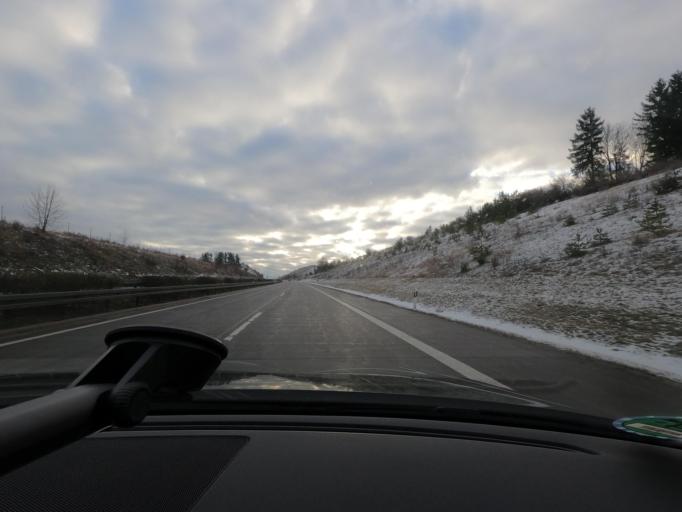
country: DE
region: Thuringia
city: Veilsdorf
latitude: 50.4701
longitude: 10.8296
